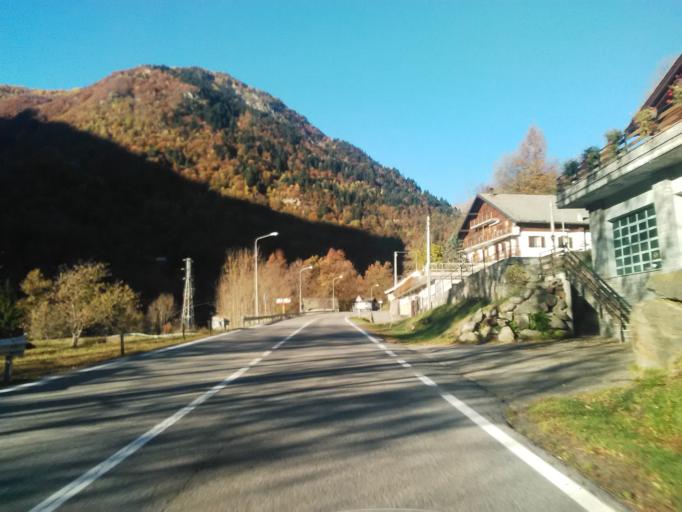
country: IT
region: Piedmont
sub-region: Provincia di Vercelli
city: Piode
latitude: 45.7694
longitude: 8.0578
